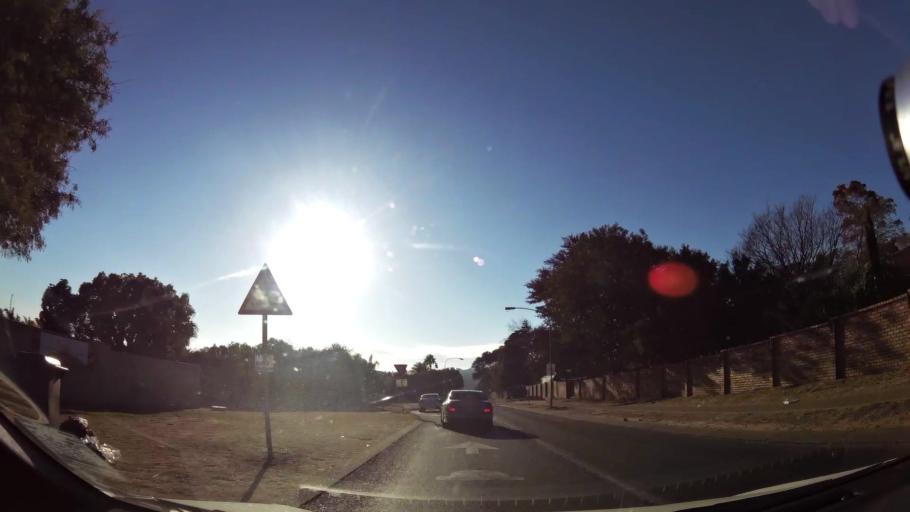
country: ZA
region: Gauteng
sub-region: City of Tshwane Metropolitan Municipality
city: Centurion
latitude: -25.8945
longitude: 28.1333
